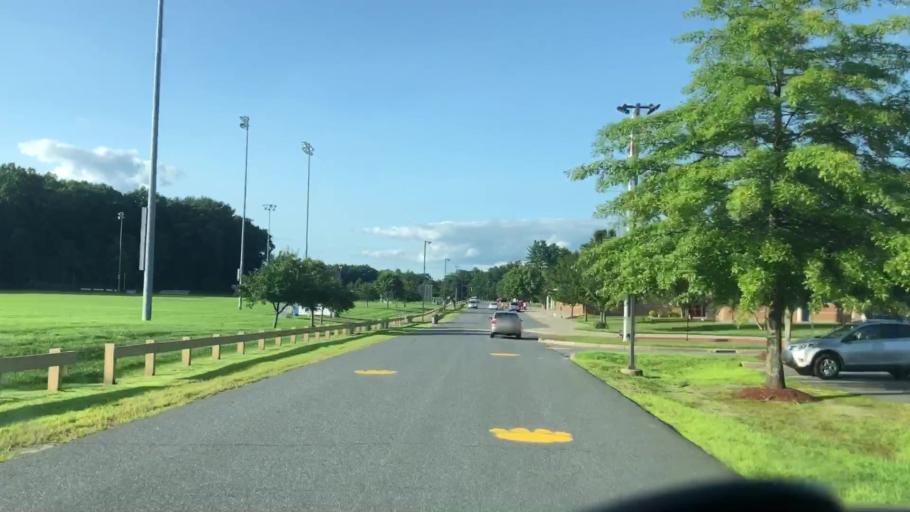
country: US
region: Massachusetts
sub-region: Franklin County
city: Northfield
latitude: 42.6827
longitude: -72.4862
